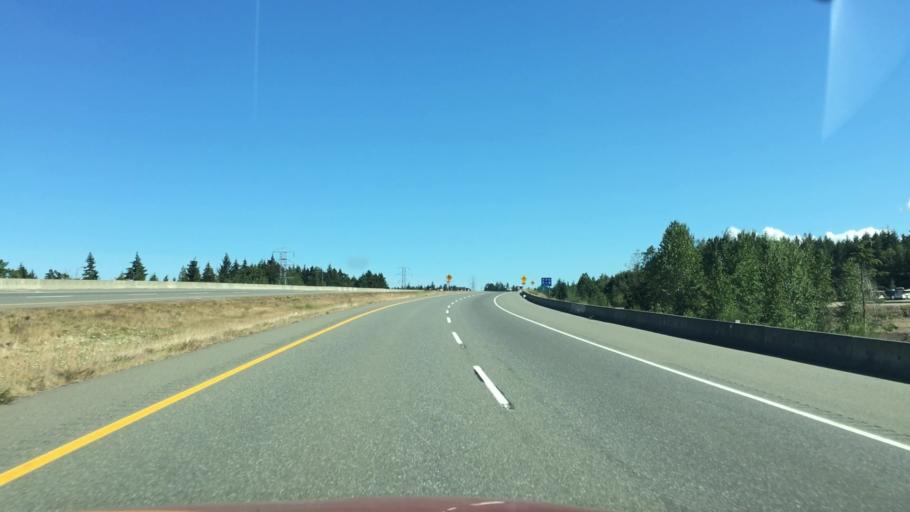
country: CA
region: British Columbia
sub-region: Regional District of Nanaimo
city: Parksville
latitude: 49.3119
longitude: -124.3458
